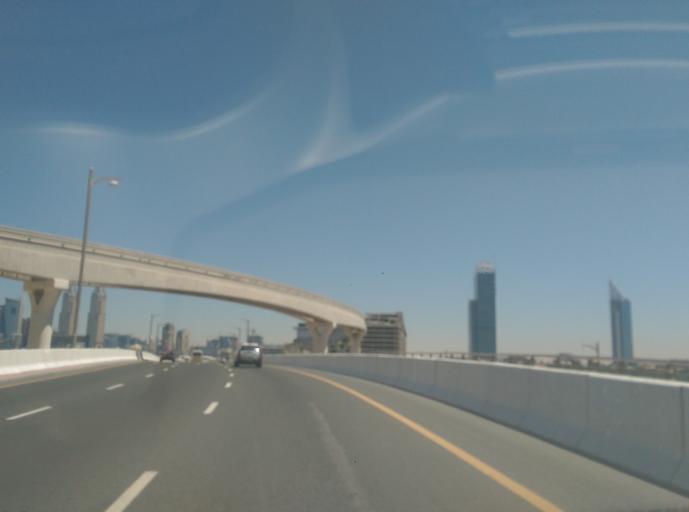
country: AE
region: Dubai
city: Dubai
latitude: 25.1043
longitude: 55.1495
